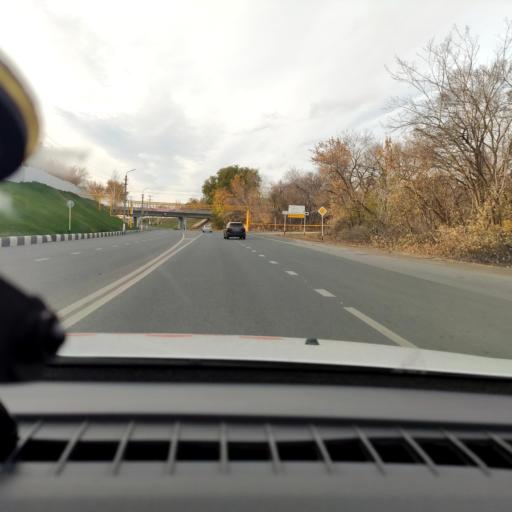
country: RU
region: Samara
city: Novokuybyshevsk
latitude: 53.1199
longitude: 49.9394
